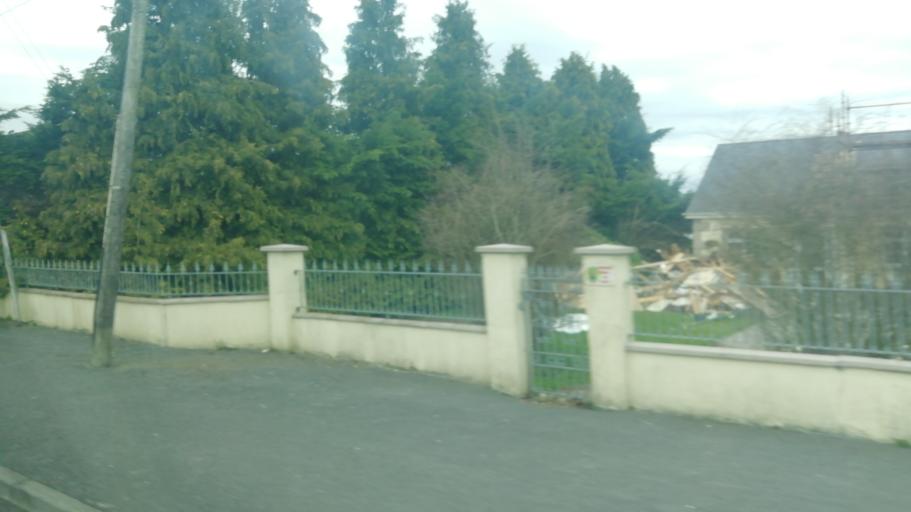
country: IE
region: Leinster
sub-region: Uibh Fhaili
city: Edenderry
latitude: 53.3351
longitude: -7.0414
